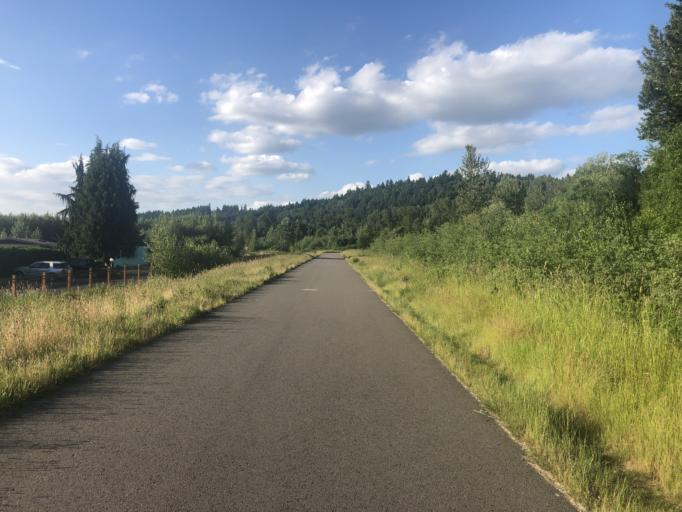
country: US
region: Washington
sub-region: King County
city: Lea Hill
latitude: 47.3399
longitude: -122.2098
